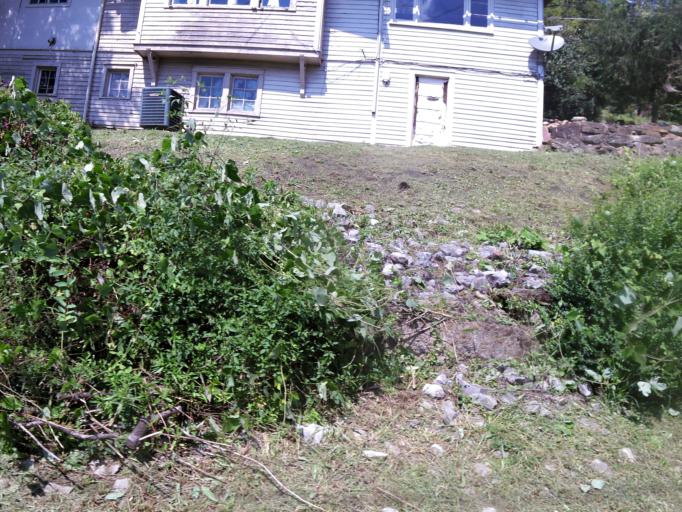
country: US
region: Kentucky
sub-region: Harlan County
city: Harlan
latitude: 36.8482
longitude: -83.3180
